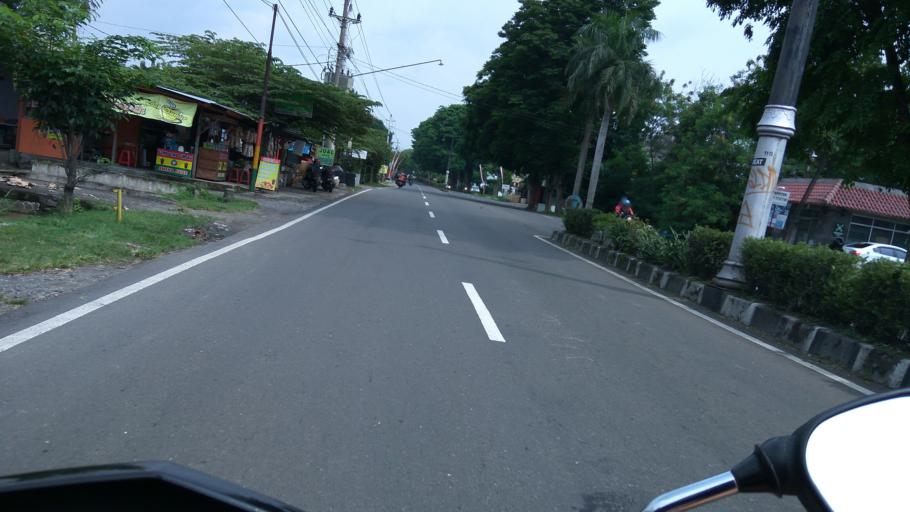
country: ID
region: Central Java
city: Jaten
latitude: -7.5878
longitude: 110.9218
